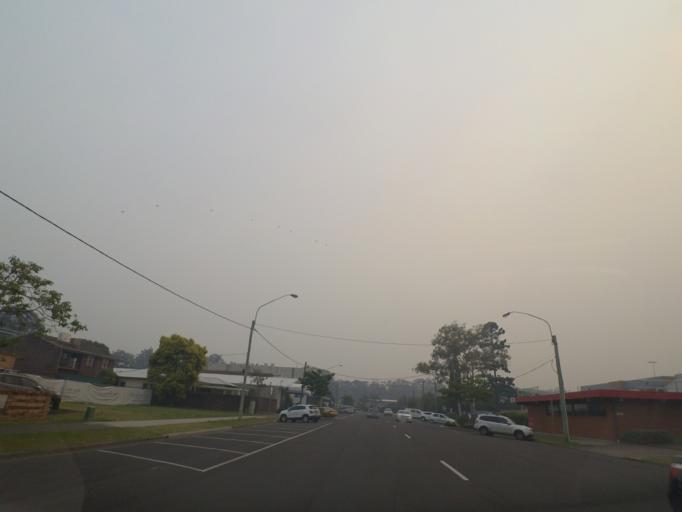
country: AU
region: New South Wales
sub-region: Coffs Harbour
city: Coffs Harbour
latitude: -30.2967
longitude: 153.1175
